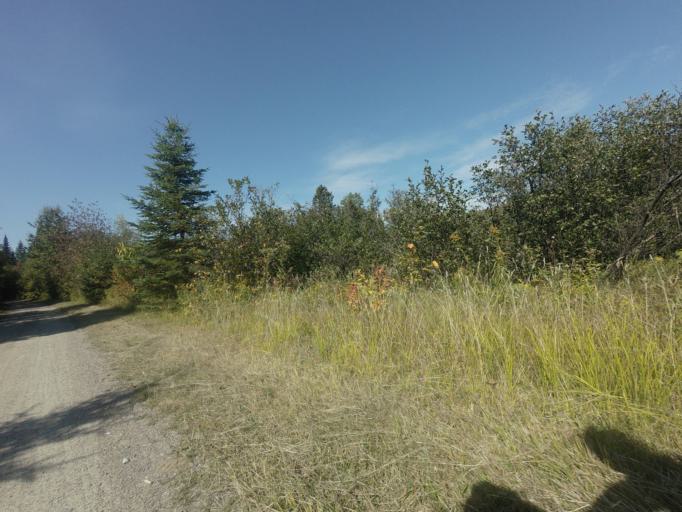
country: CA
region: Quebec
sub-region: Laurentides
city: Sainte-Agathe-des-Monts
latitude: 46.1056
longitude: -74.4003
